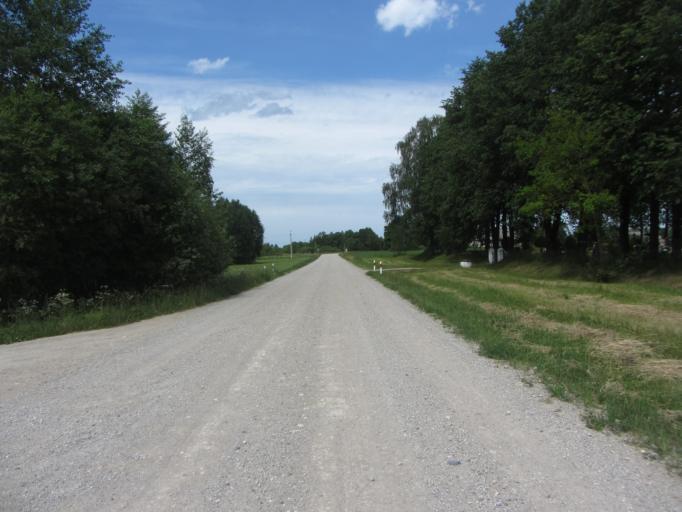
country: LT
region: Panevezys
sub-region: Birzai
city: Birzai
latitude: 56.1691
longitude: 24.9394
